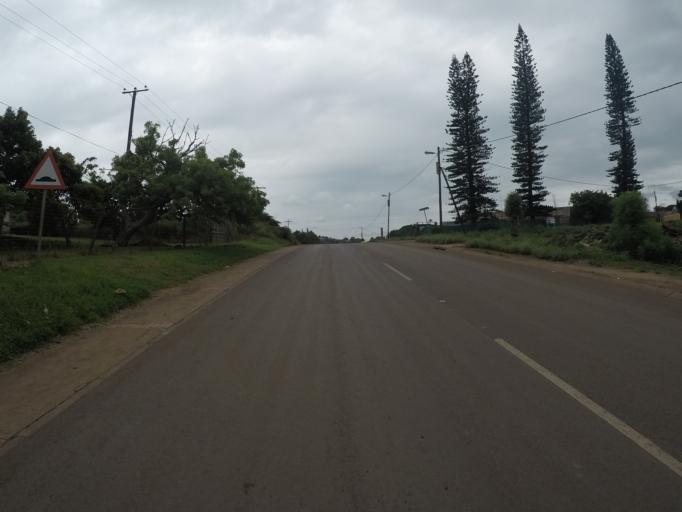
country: ZA
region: KwaZulu-Natal
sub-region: uThungulu District Municipality
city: Empangeni
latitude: -28.7725
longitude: 31.8548
